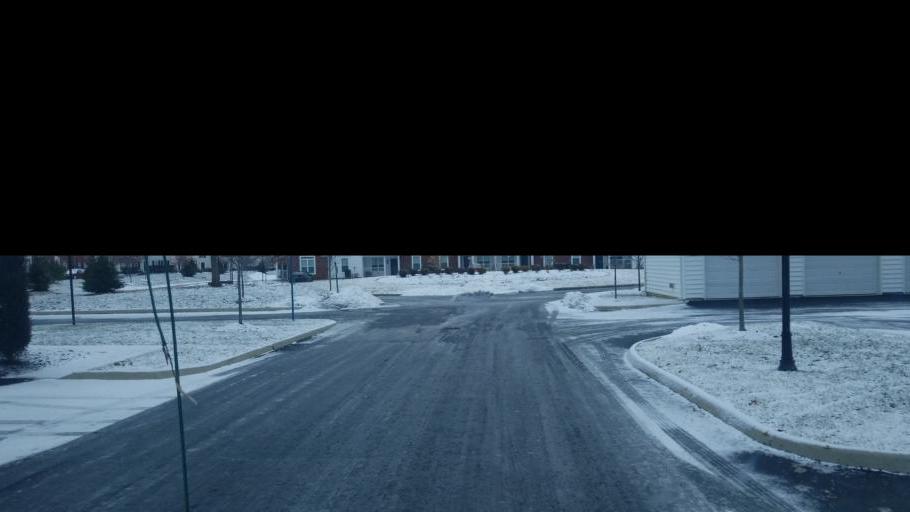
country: US
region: Ohio
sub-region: Franklin County
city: New Albany
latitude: 40.0592
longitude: -82.8460
